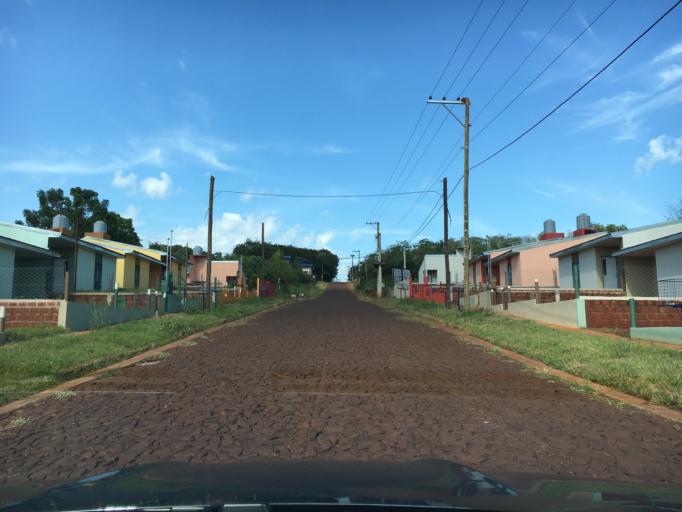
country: AR
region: Misiones
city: Puerto Rico
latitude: -26.8170
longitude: -55.0361
